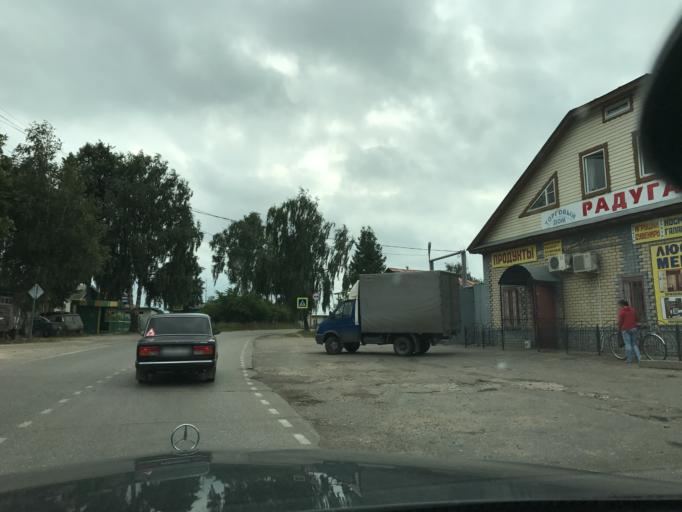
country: RU
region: Nizjnij Novgorod
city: Pavlovo
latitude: 55.9955
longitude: 43.0412
